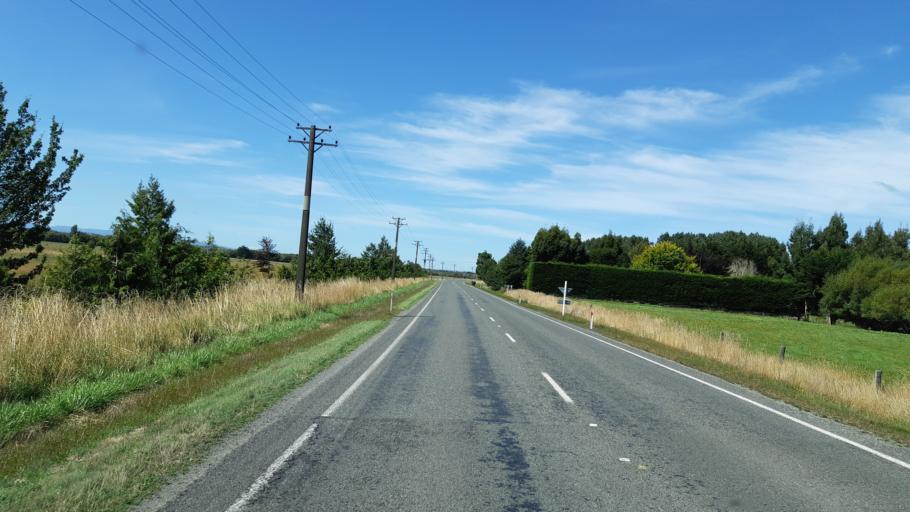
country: NZ
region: Southland
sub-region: Gore District
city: Gore
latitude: -45.9940
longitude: 168.8169
